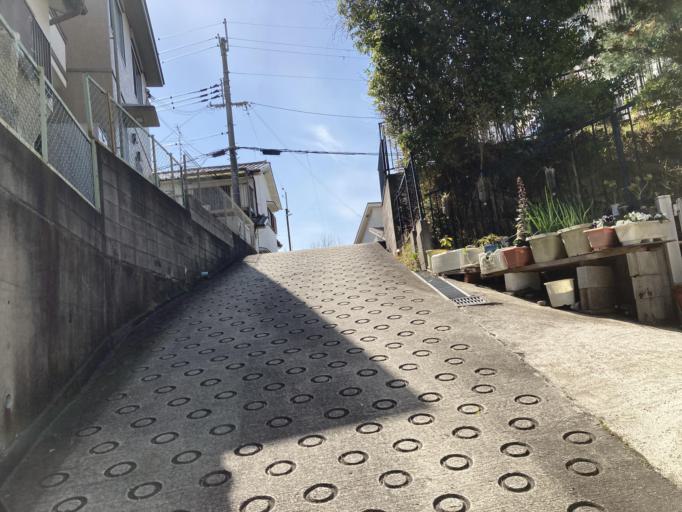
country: JP
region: Nara
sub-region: Ikoma-shi
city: Ikoma
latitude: 34.6845
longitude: 135.7126
